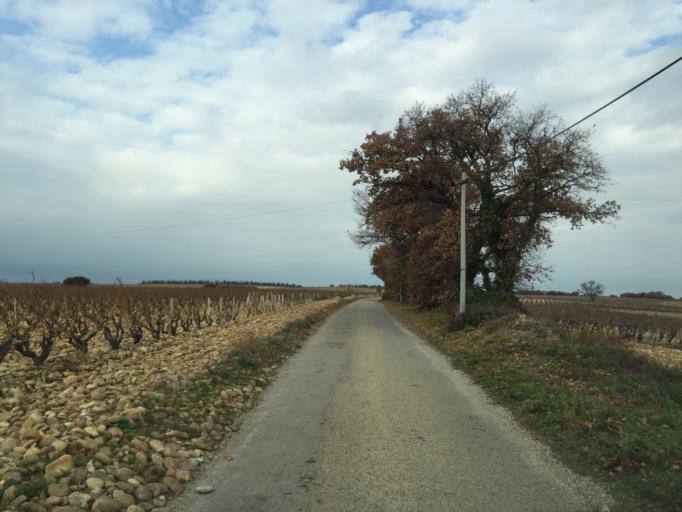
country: FR
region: Provence-Alpes-Cote d'Azur
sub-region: Departement du Vaucluse
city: Bedarrides
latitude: 44.0502
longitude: 4.8721
